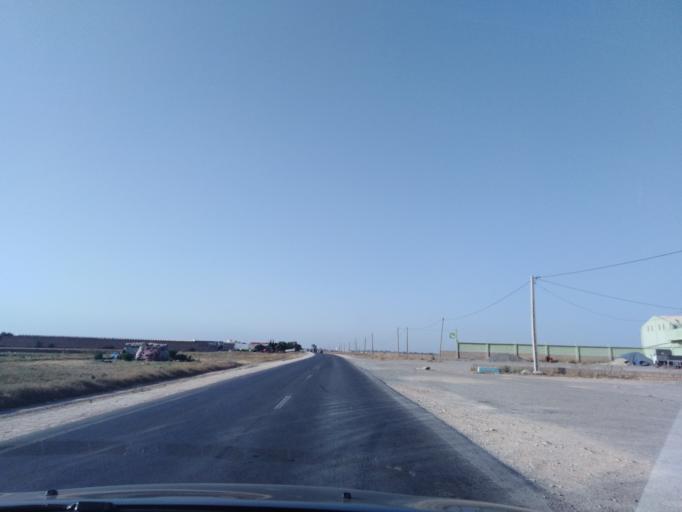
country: MA
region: Doukkala-Abda
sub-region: El-Jadida
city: Sidi Bennour
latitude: 32.5916
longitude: -8.7088
